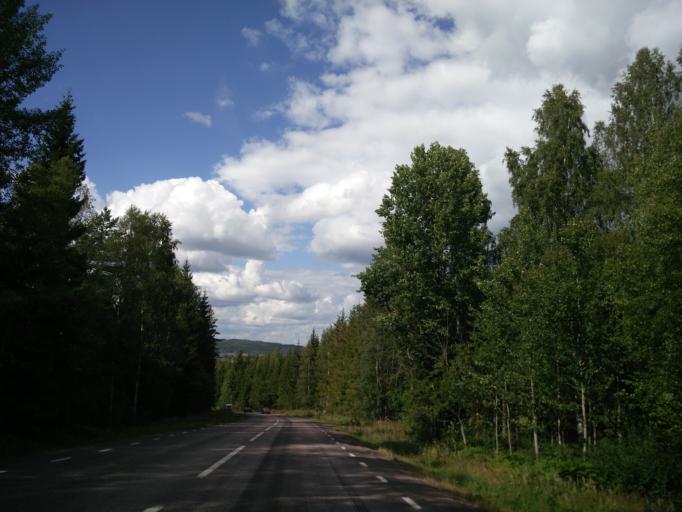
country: SE
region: Vaermland
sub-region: Sunne Kommun
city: Sunne
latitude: 59.7064
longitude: 13.1063
